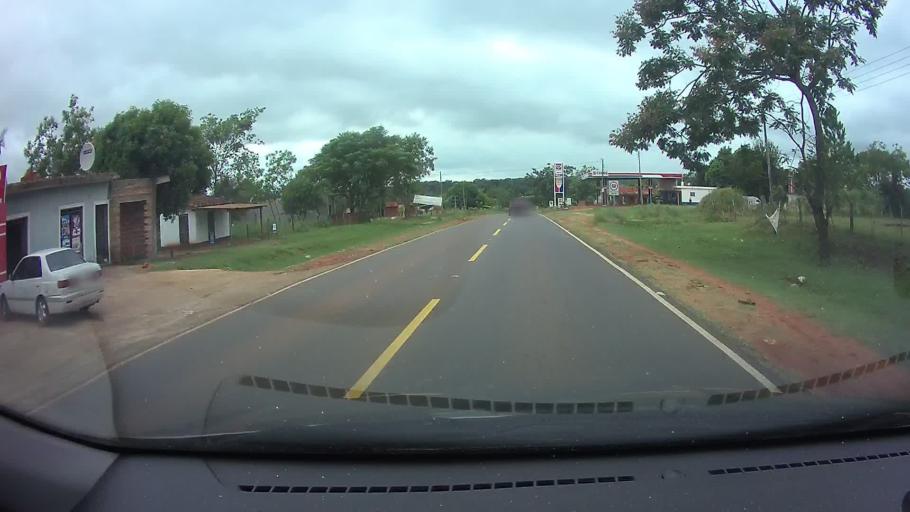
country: PY
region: Paraguari
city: Carapegua
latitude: -25.7341
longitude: -57.3011
